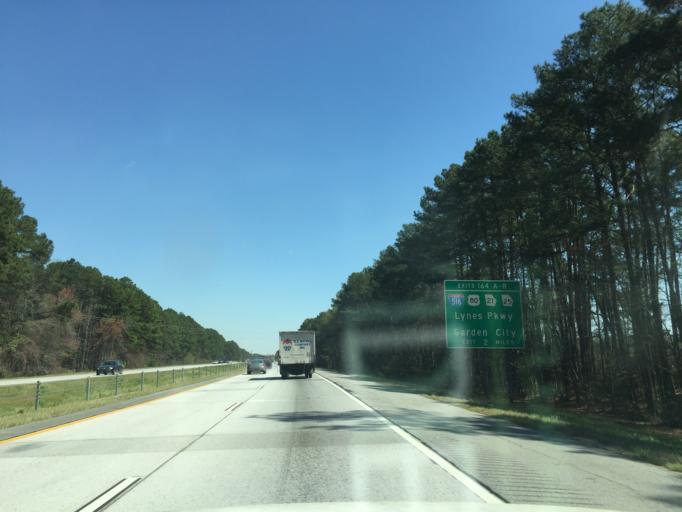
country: US
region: Georgia
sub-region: Chatham County
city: Garden City
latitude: 32.0679
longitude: -81.1711
